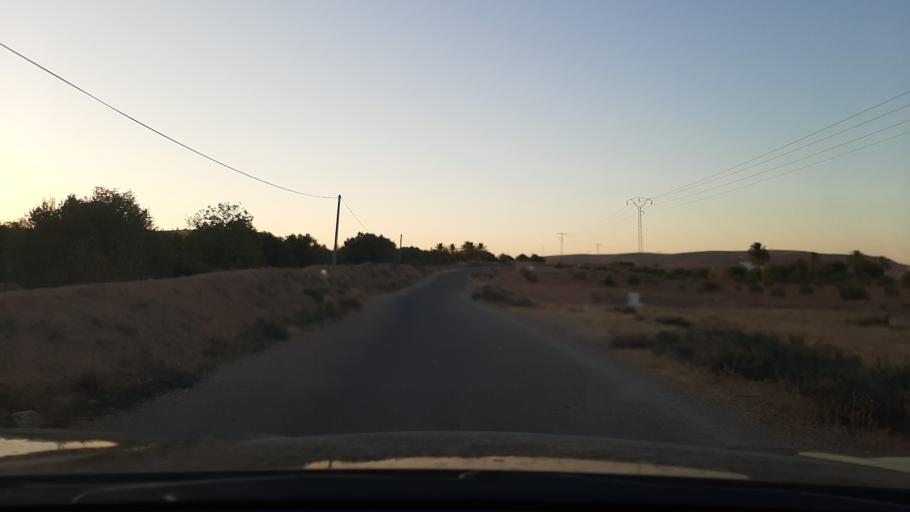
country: TN
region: Qabis
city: Matmata
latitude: 33.5568
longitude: 10.1847
